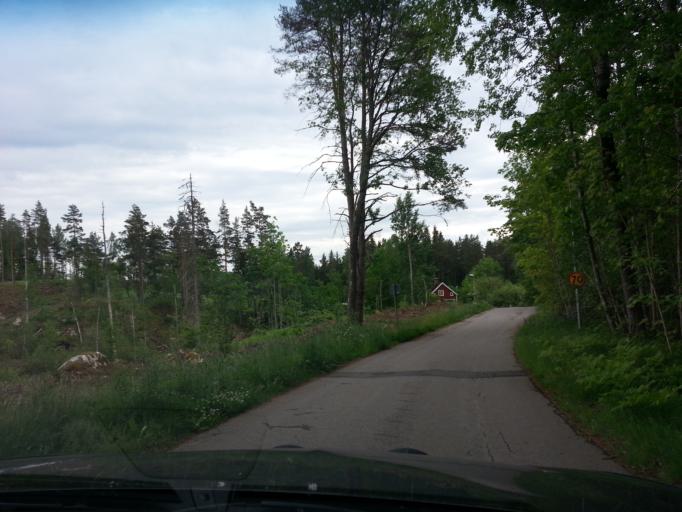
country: SE
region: Joenkoeping
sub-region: Vetlanda Kommun
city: Vetlanda
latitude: 57.2911
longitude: 15.1272
